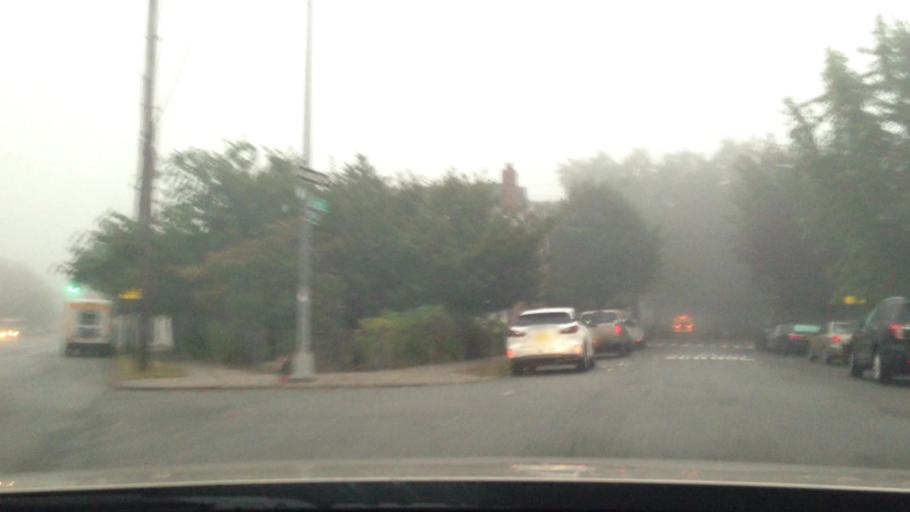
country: US
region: New York
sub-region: Kings County
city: Brooklyn
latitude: 40.6061
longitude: -73.9400
